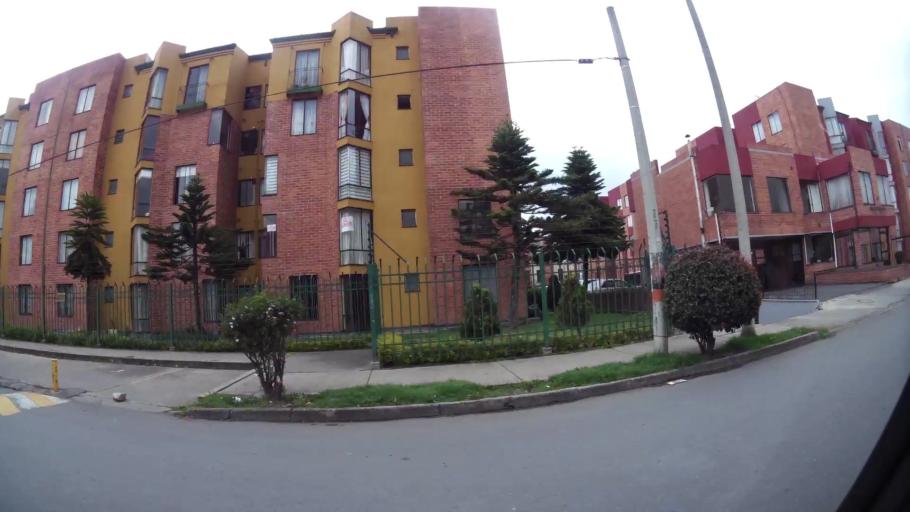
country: CO
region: Cundinamarca
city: Cota
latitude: 4.7460
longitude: -74.0558
